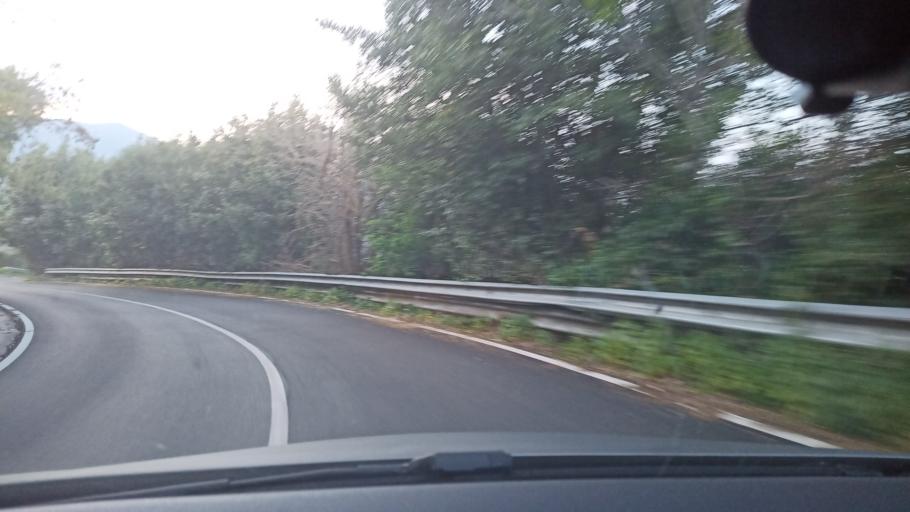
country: IT
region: Latium
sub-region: Provincia di Rieti
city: Torri in Sabina
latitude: 42.3328
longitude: 12.6451
